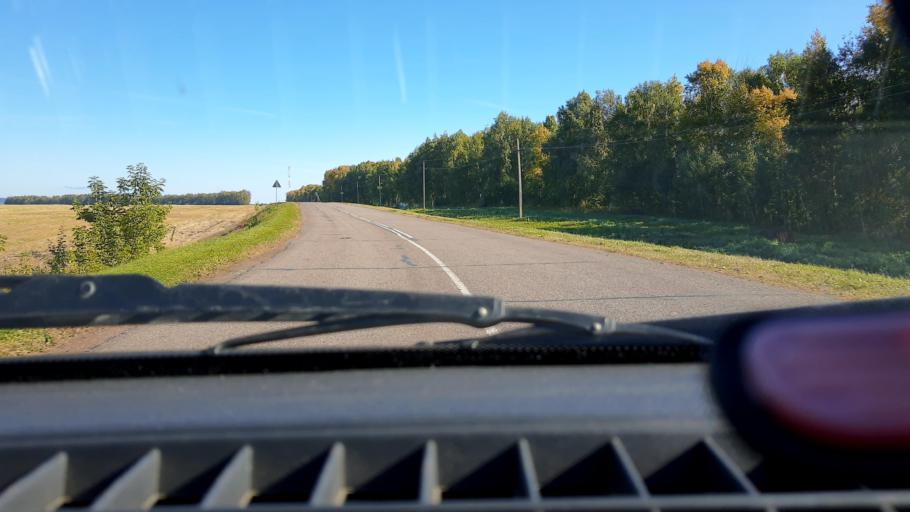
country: RU
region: Bashkortostan
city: Kushnarenkovo
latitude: 55.0637
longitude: 55.4464
